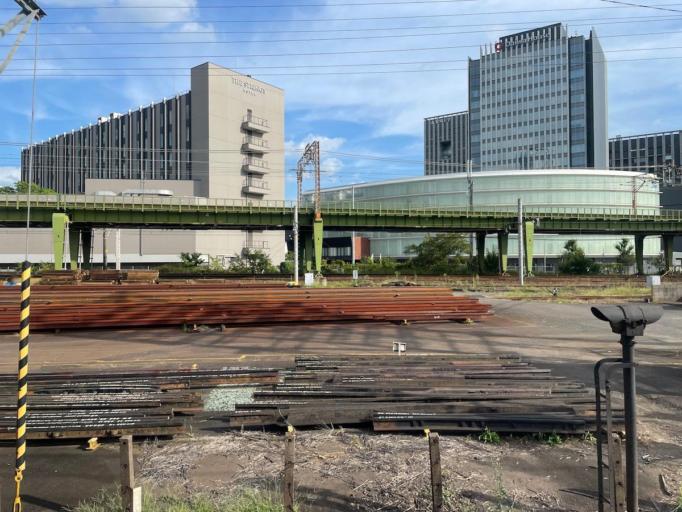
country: JP
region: Aichi
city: Nagoya-shi
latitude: 35.1639
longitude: 136.8829
